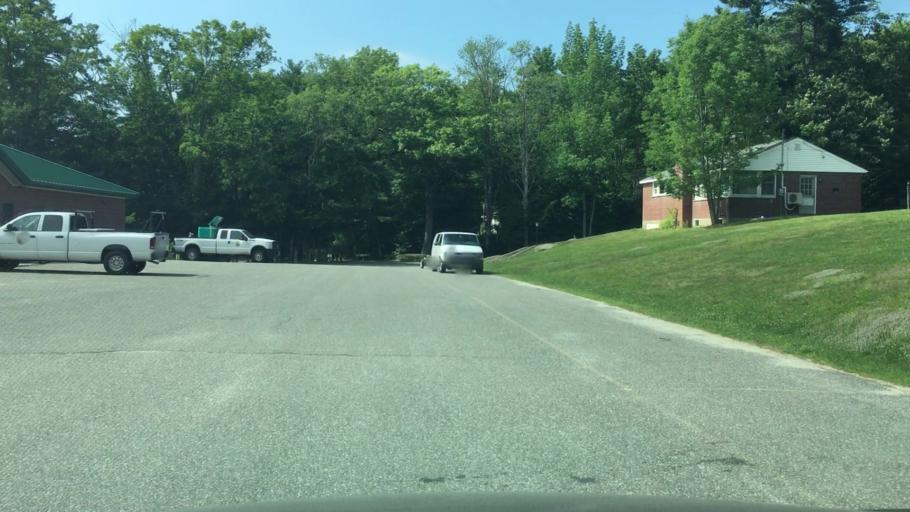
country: US
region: Maine
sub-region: Hancock County
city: Orland
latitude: 44.5853
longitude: -68.6888
